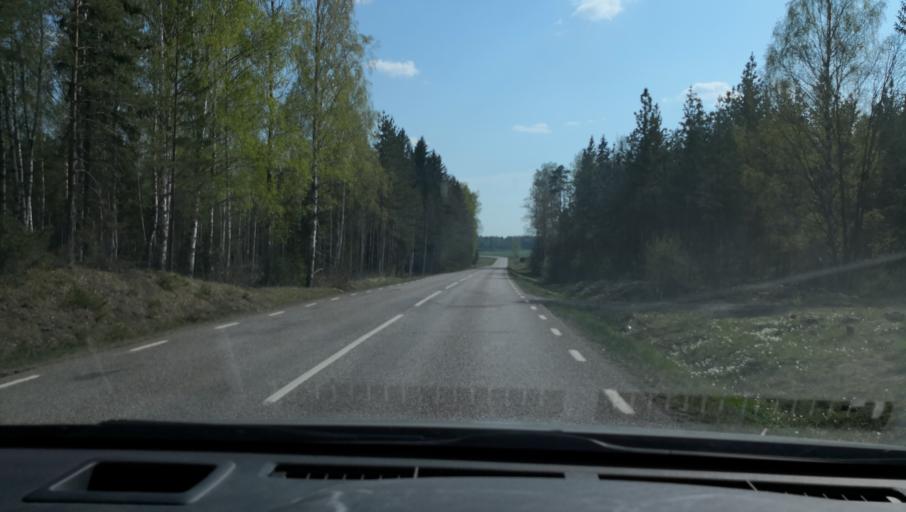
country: SE
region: Vaestmanland
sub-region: Sala Kommun
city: Sala
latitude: 59.9989
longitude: 16.6420
